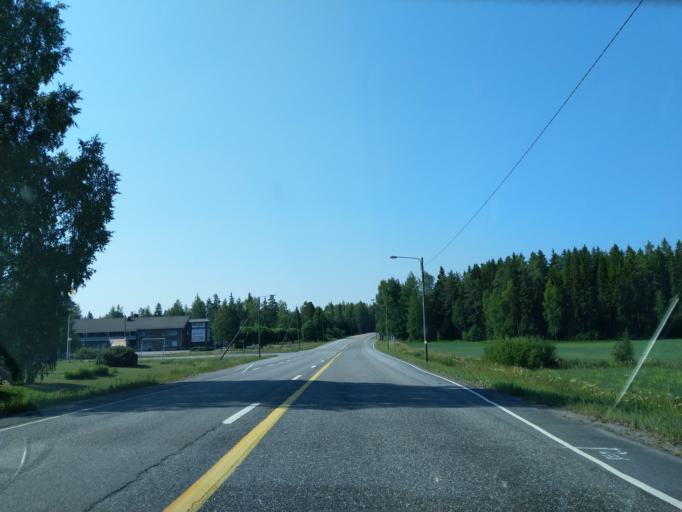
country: FI
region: Satakunta
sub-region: Pori
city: Noormarkku
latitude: 61.5854
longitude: 21.8518
